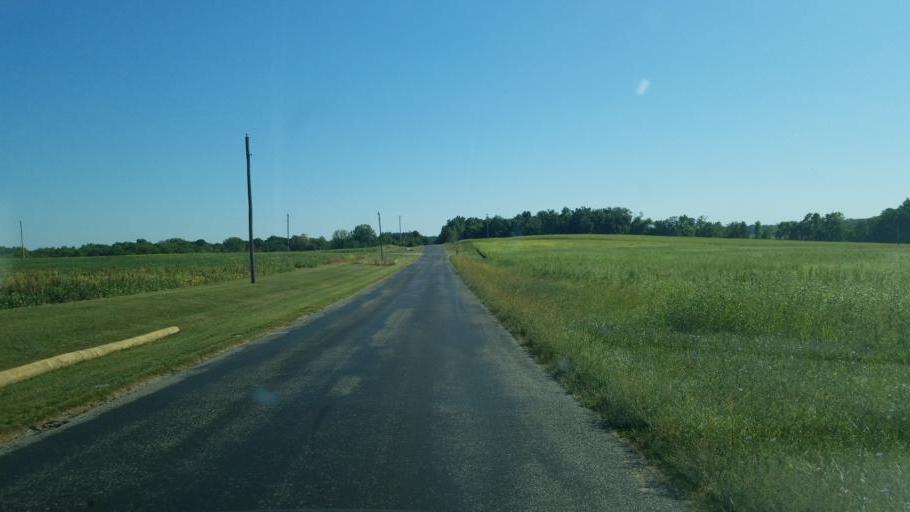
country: US
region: Ohio
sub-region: Champaign County
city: North Lewisburg
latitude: 40.1831
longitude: -83.6163
